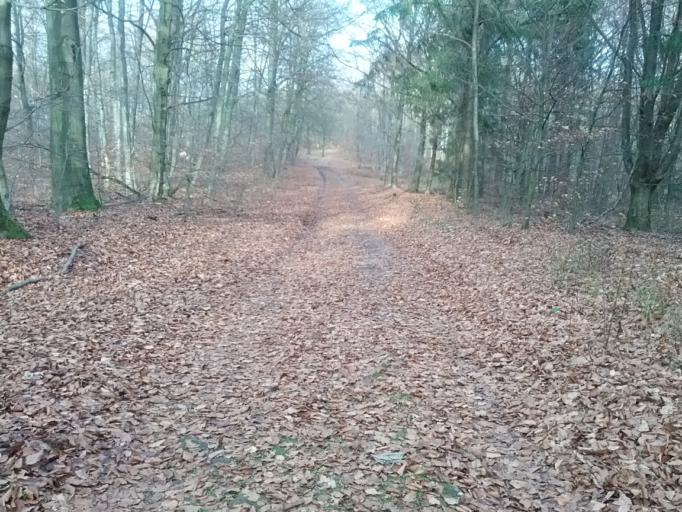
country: DE
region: Thuringia
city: Eisenach
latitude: 50.9292
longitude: 10.3206
